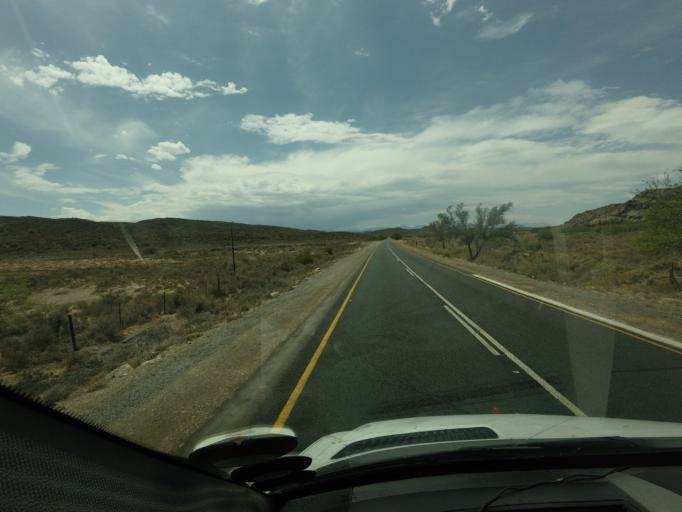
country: ZA
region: Western Cape
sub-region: Eden District Municipality
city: Ladismith
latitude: -33.7521
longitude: 20.9485
